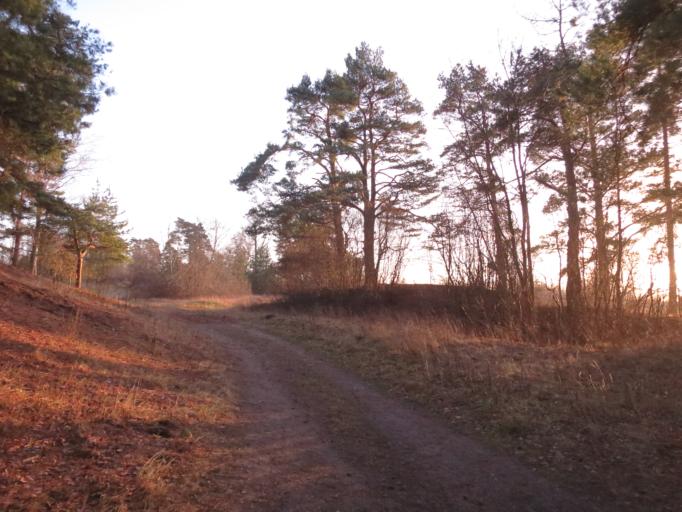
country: LV
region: Riga
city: Bergi
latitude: 56.9745
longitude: 24.3056
